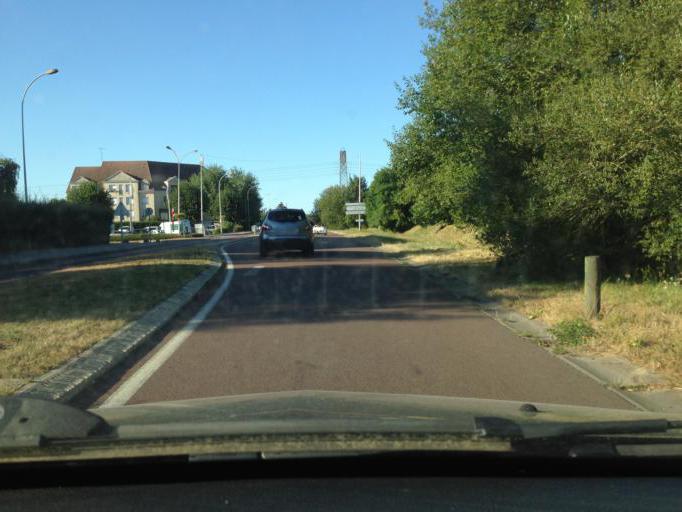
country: FR
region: Ile-de-France
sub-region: Departement des Yvelines
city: Saint-Remy-les-Chevreuse
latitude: 48.7151
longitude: 2.0856
